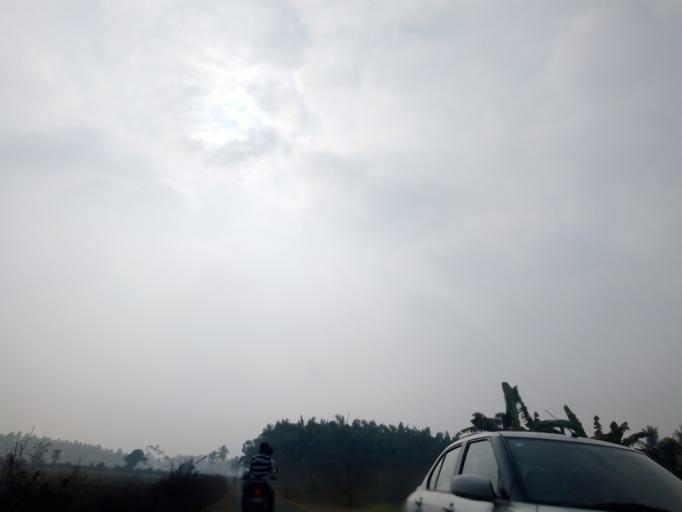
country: IN
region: Andhra Pradesh
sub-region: West Godavari
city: Tadepallegudem
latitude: 16.8468
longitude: 81.3380
